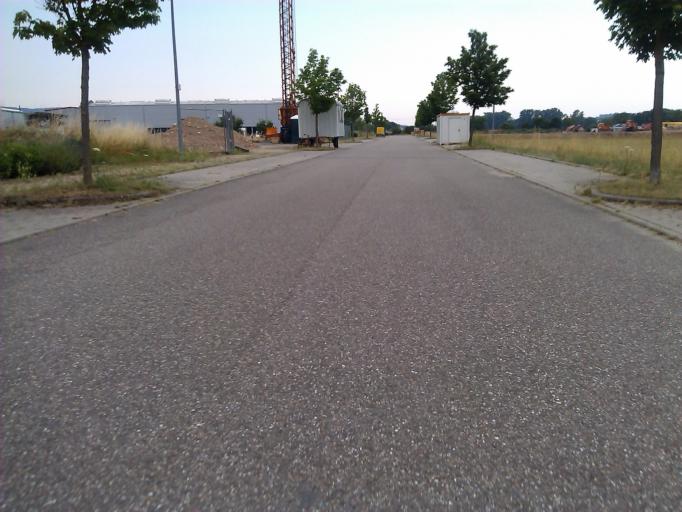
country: DE
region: Baden-Wuerttemberg
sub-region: Regierungsbezirk Stuttgart
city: Cleebronn
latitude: 49.0665
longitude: 9.0412
